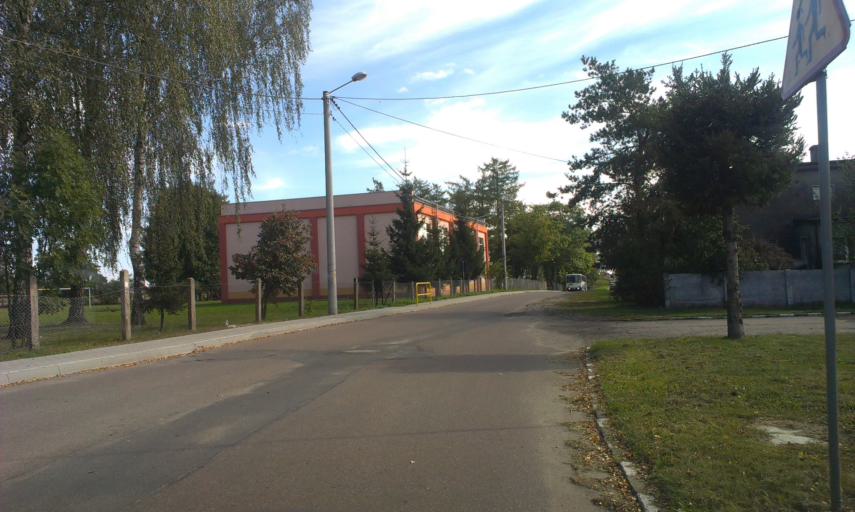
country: PL
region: Greater Poland Voivodeship
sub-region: Powiat zlotowski
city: Zlotow
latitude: 53.3062
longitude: 17.1319
